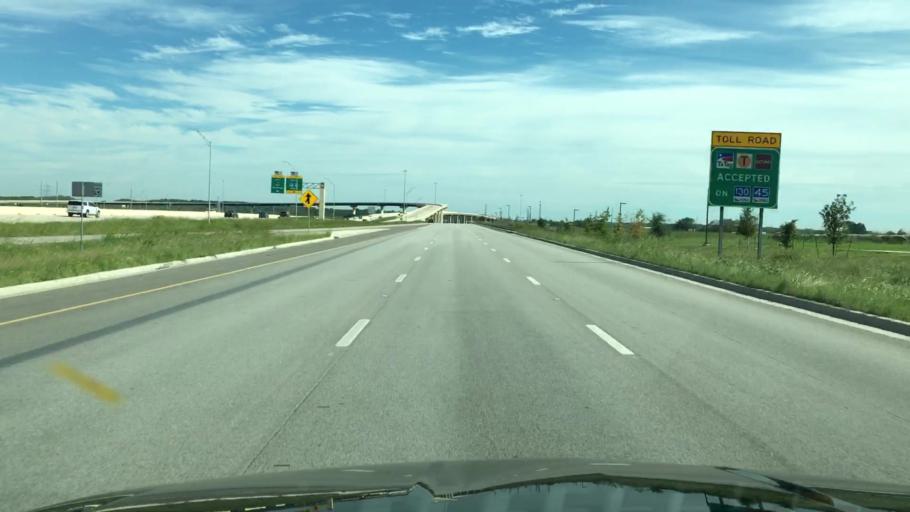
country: US
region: Texas
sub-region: Travis County
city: Hornsby Bend
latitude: 30.2004
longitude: -97.6354
